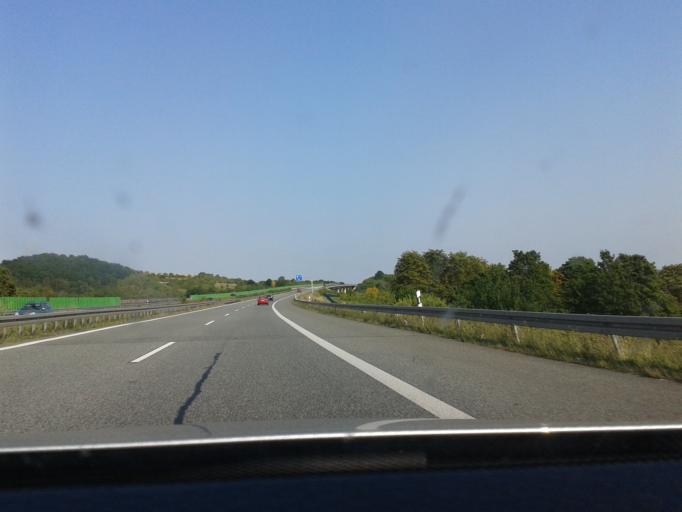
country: DE
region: Saxony-Anhalt
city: Rossla
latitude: 51.4749
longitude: 11.0731
